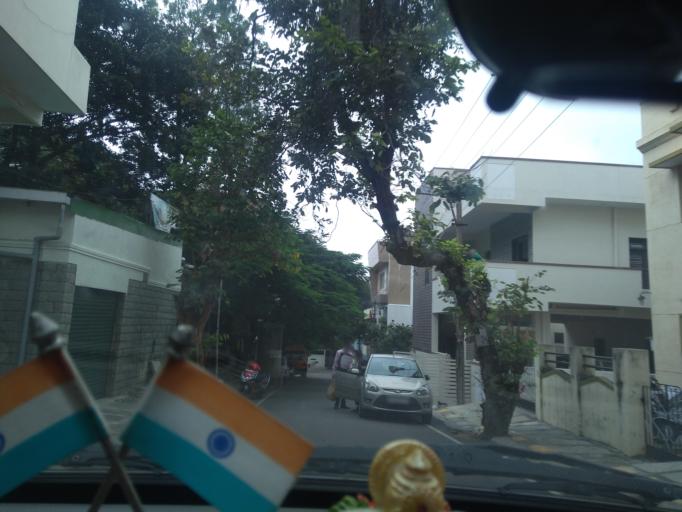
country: IN
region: Karnataka
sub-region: Bangalore Urban
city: Bangalore
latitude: 12.9841
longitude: 77.5514
